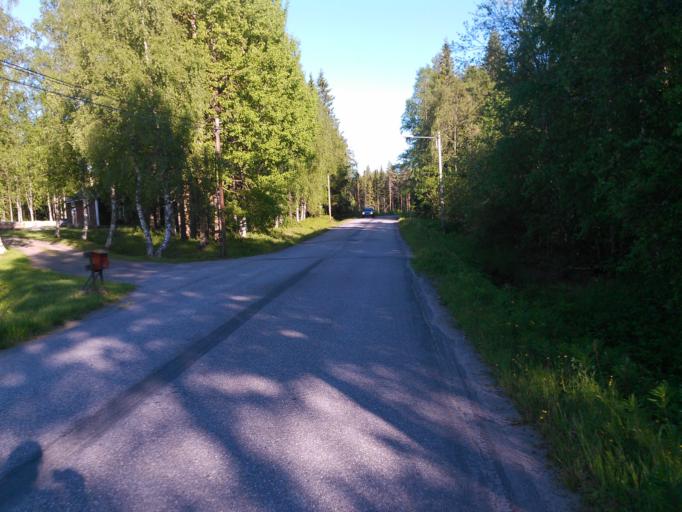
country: SE
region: Vaesterbotten
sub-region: Umea Kommun
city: Ersmark
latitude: 63.8770
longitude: 20.3224
